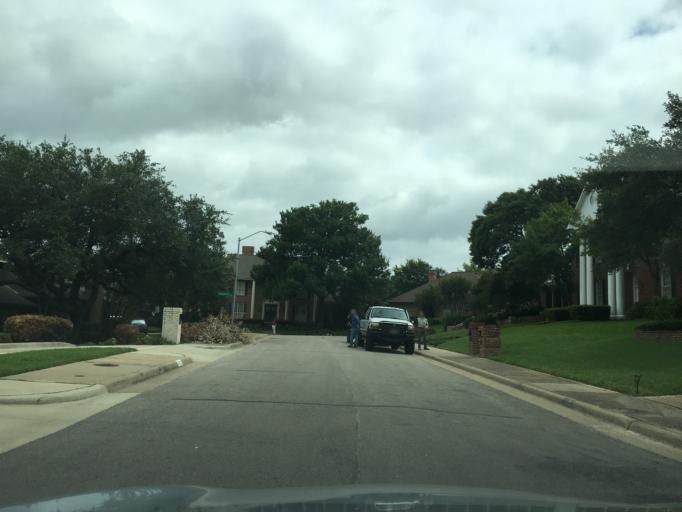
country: US
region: Texas
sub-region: Dallas County
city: University Park
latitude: 32.8792
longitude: -96.7423
